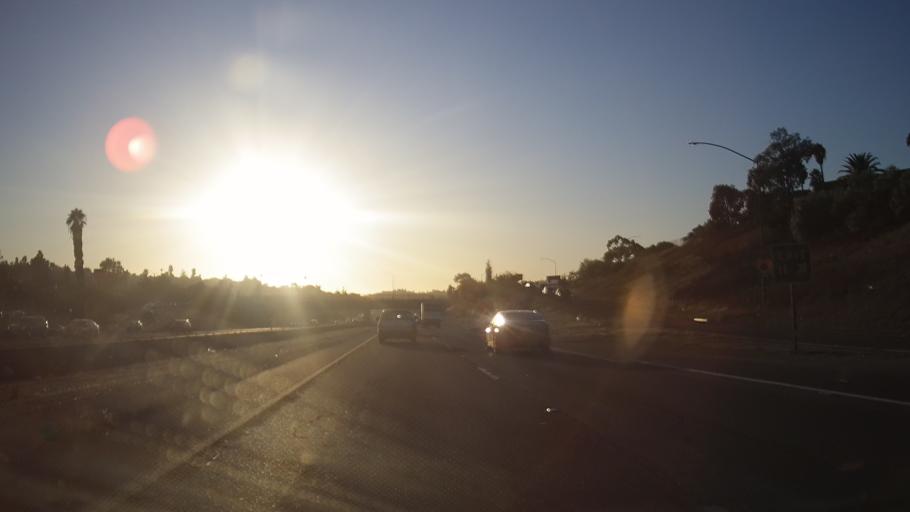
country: US
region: California
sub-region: San Diego County
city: Casa de Oro-Mount Helix
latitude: 32.7447
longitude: -116.9717
